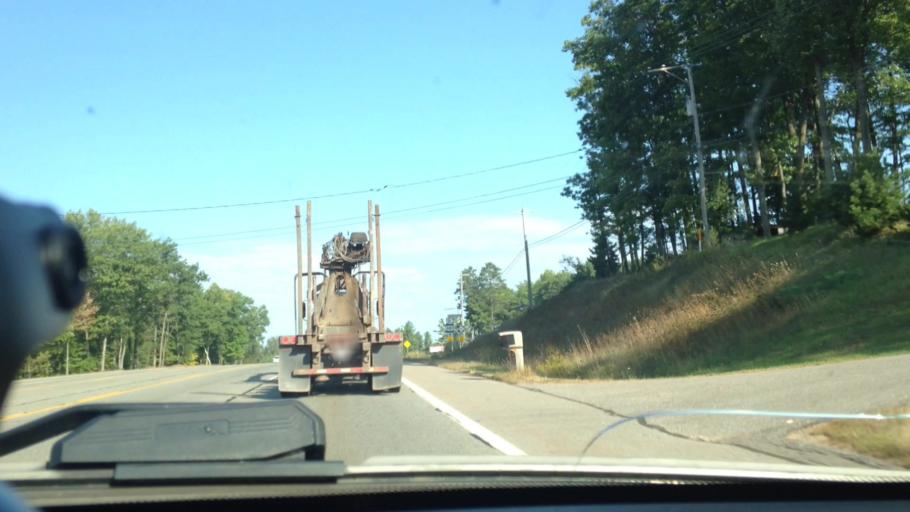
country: US
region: Michigan
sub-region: Dickinson County
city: Iron Mountain
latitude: 45.8565
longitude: -88.0579
